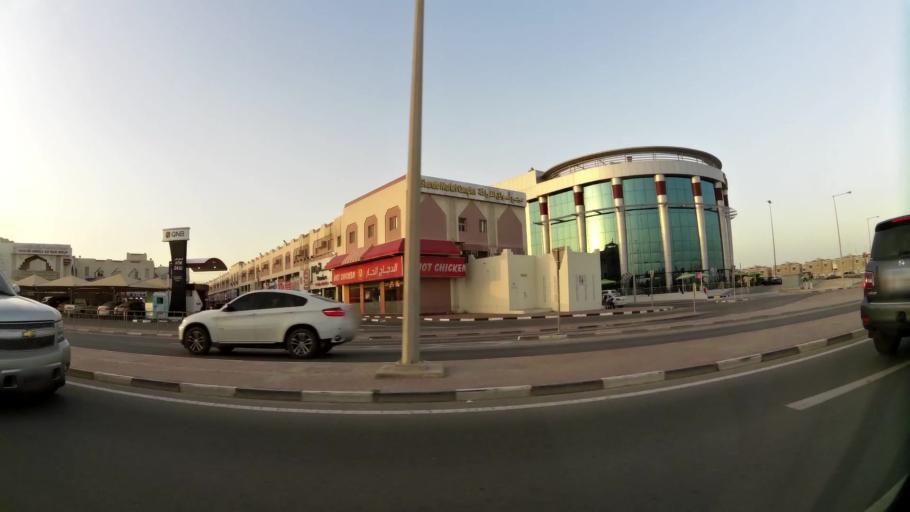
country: QA
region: Baladiyat ar Rayyan
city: Ar Rayyan
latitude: 25.3262
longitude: 51.4658
